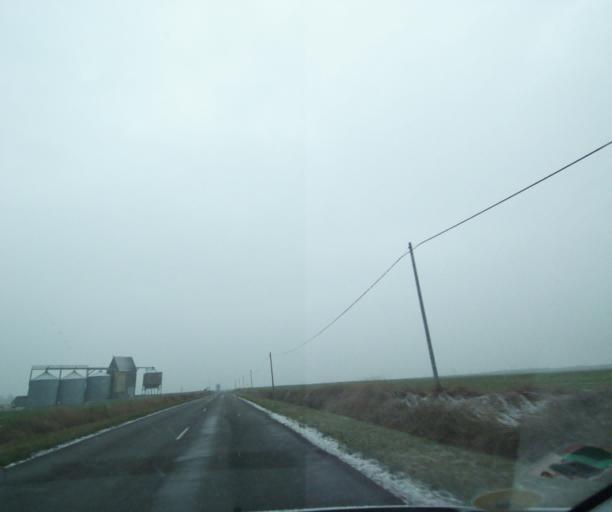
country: FR
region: Champagne-Ardenne
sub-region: Departement de la Haute-Marne
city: Wassy
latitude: 48.4857
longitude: 4.9837
